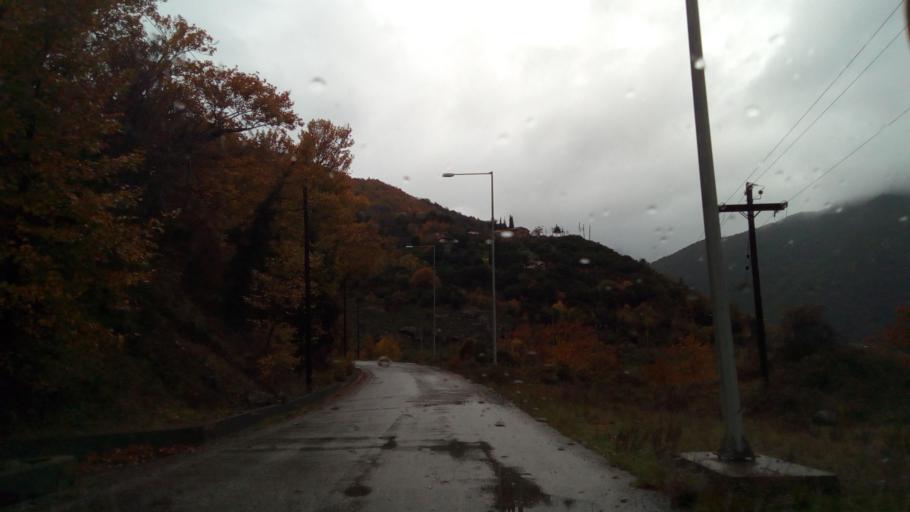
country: GR
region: West Greece
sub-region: Nomos Aitolias kai Akarnanias
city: Thermo
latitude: 38.6615
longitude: 21.8425
